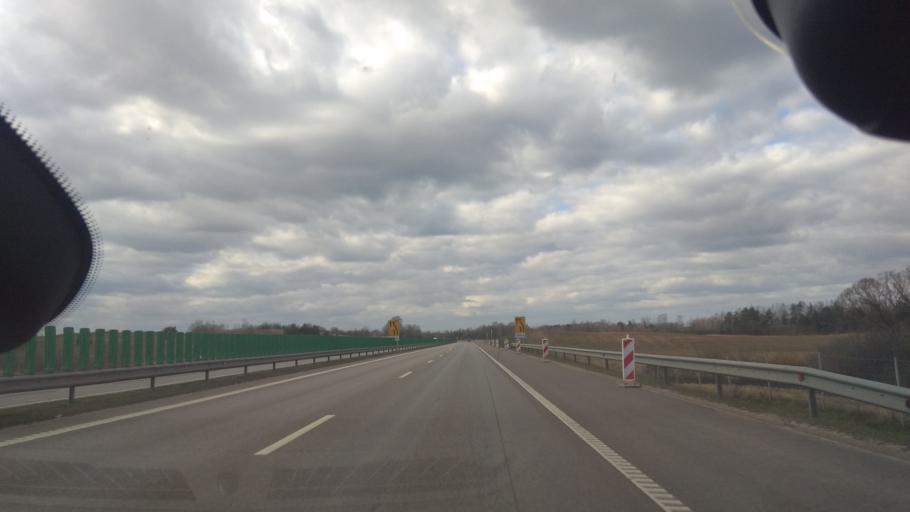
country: LT
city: Trakai
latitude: 54.7362
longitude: 24.9528
